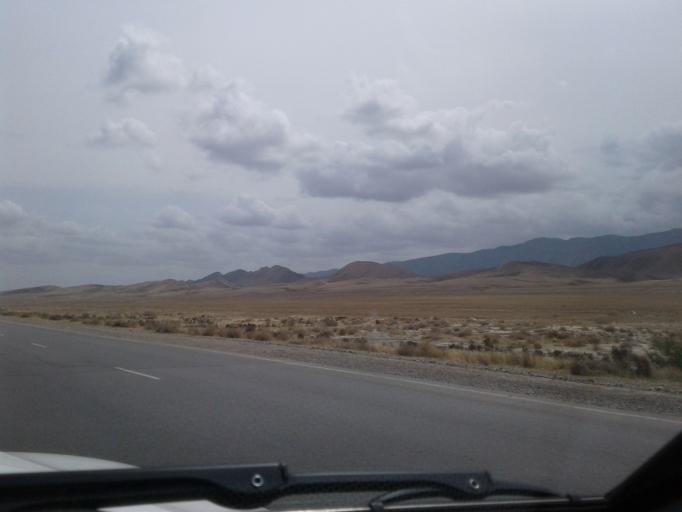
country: IR
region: Razavi Khorasan
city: Dargaz
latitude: 37.6990
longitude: 59.0456
